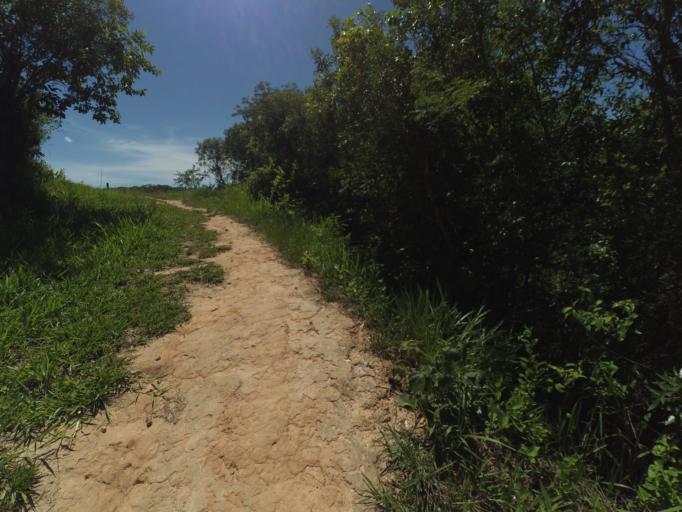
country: BO
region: Chuquisaca
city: Monteagudo
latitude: -19.8027
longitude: -63.9530
